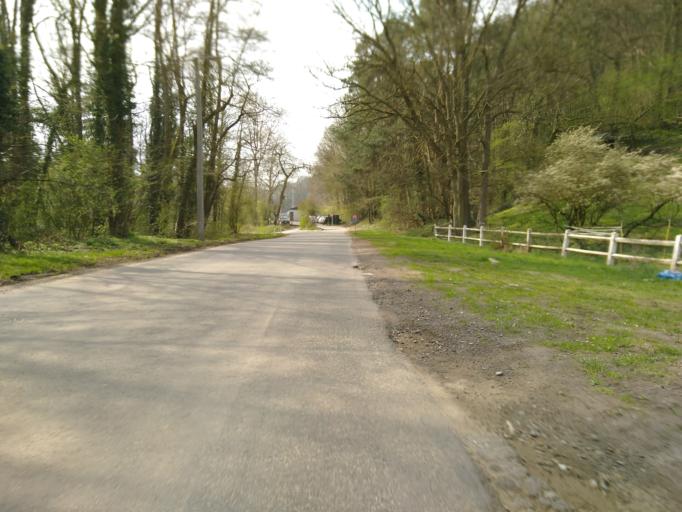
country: BE
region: Wallonia
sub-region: Province du Brabant Wallon
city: Chaumont-Gistoux
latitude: 50.6860
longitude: 4.7181
